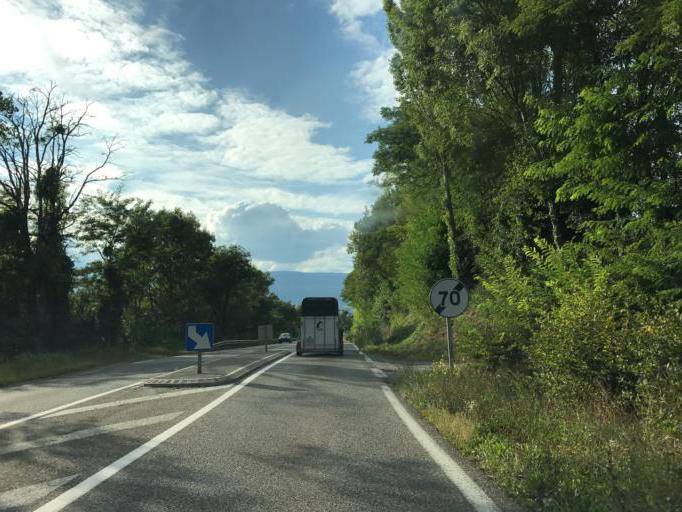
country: FR
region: Rhone-Alpes
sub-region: Departement de l'Ain
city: Bellegarde-sur-Valserine
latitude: 46.0915
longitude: 5.8587
